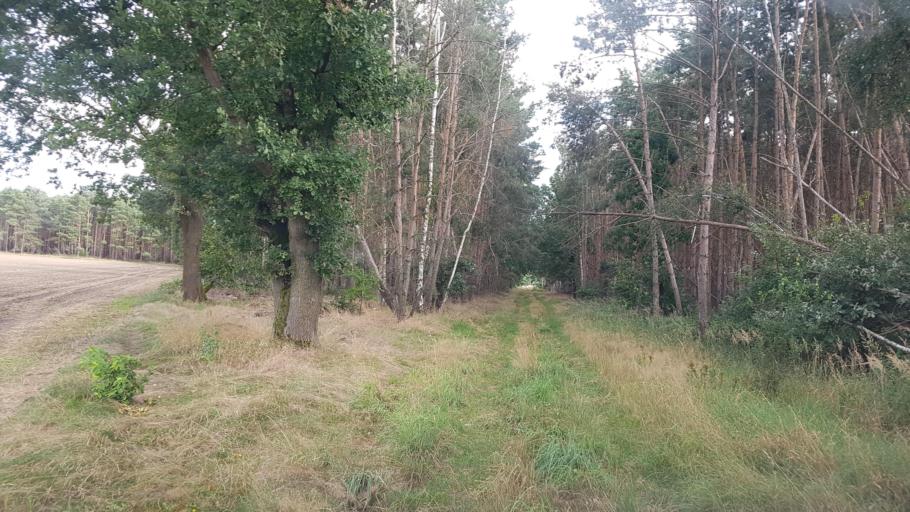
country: DE
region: Brandenburg
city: Bad Liebenwerda
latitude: 51.5056
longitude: 13.3084
